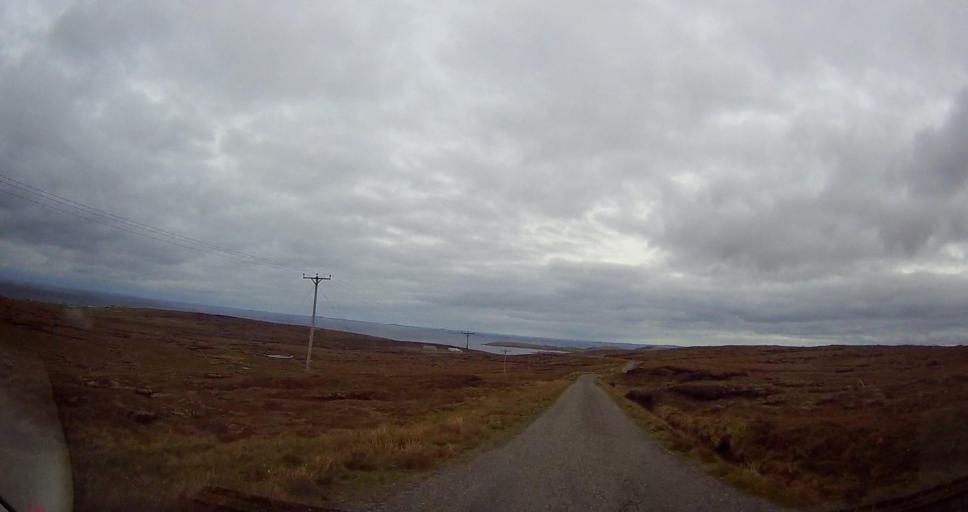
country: GB
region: Scotland
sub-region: Shetland Islands
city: Shetland
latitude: 60.5651
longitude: -1.0656
